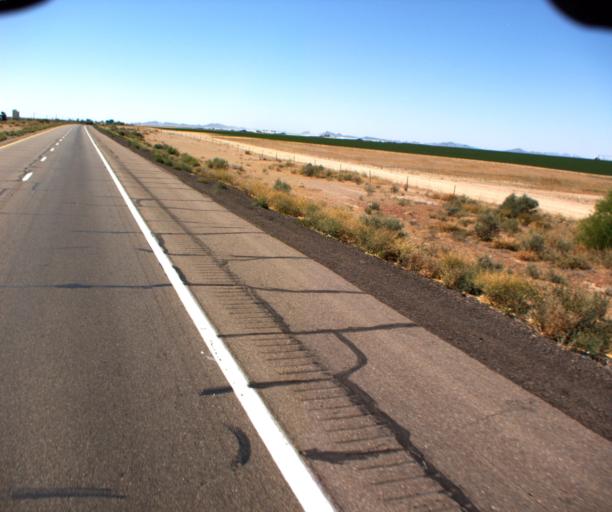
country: US
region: Arizona
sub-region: Maricopa County
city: Gila Bend
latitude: 32.9349
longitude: -112.7845
